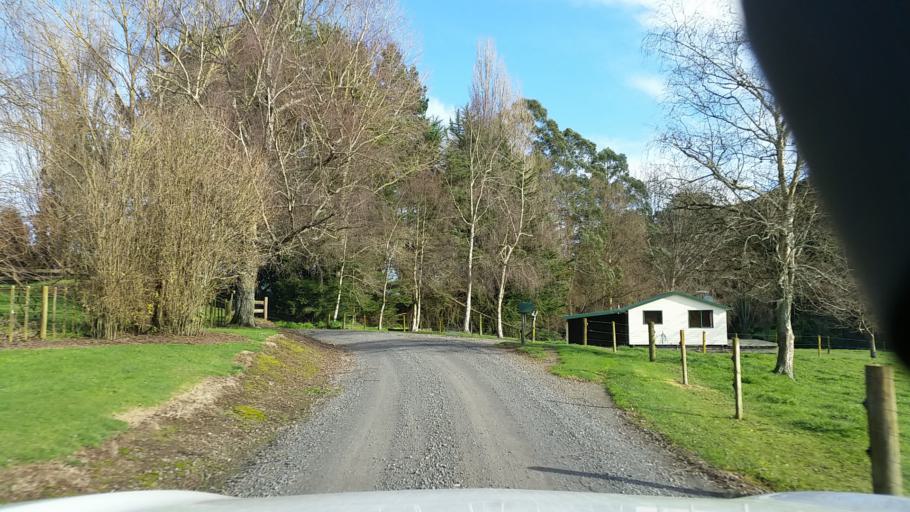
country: NZ
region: Waikato
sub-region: South Waikato District
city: Tokoroa
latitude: -38.3625
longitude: 176.0679
